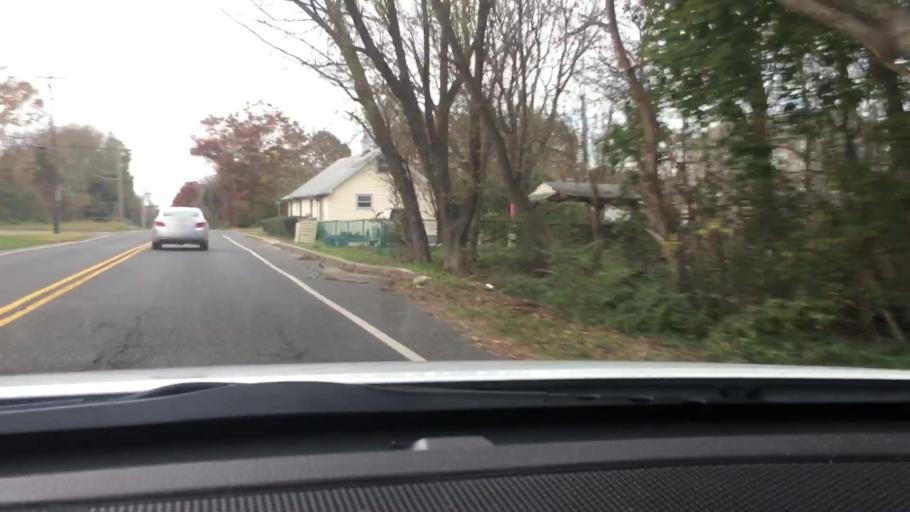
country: US
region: New Jersey
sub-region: Atlantic County
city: Northfield
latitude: 39.3880
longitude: -74.5478
